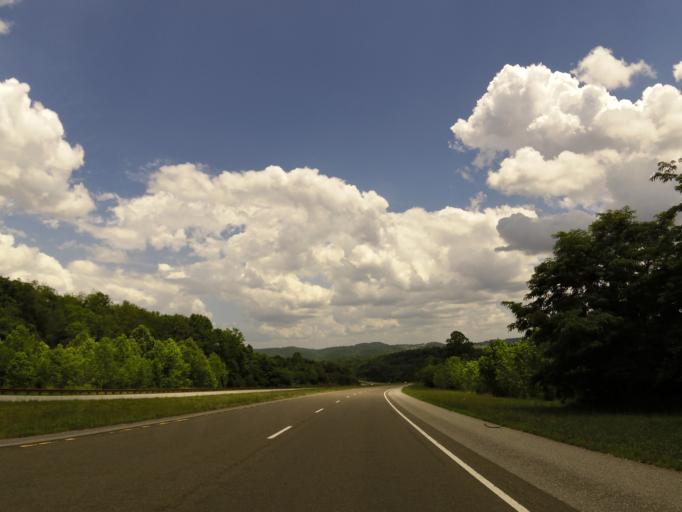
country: US
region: Tennessee
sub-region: Claiborne County
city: Harrogate
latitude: 36.6024
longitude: -83.6410
